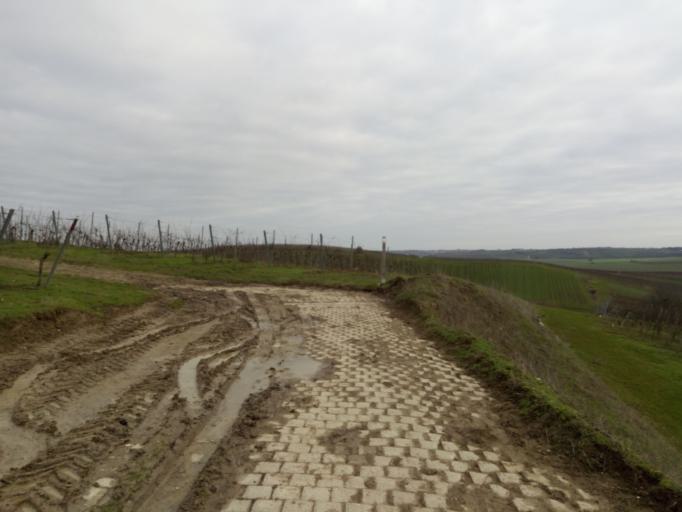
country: DE
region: Rheinland-Pfalz
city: Gau-Odernheim
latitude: 49.7932
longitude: 8.2072
